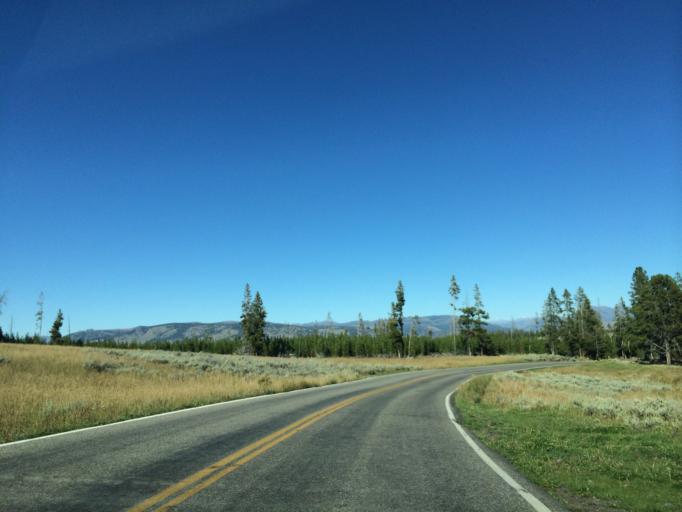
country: US
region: Montana
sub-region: Gallatin County
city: West Yellowstone
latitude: 44.8673
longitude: -110.4083
